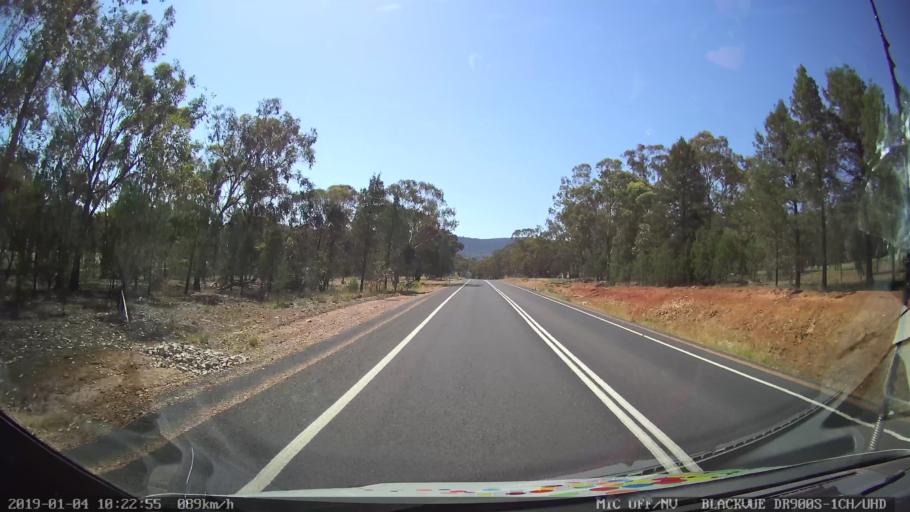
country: AU
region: New South Wales
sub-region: Cabonne
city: Canowindra
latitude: -33.3701
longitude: 148.5320
